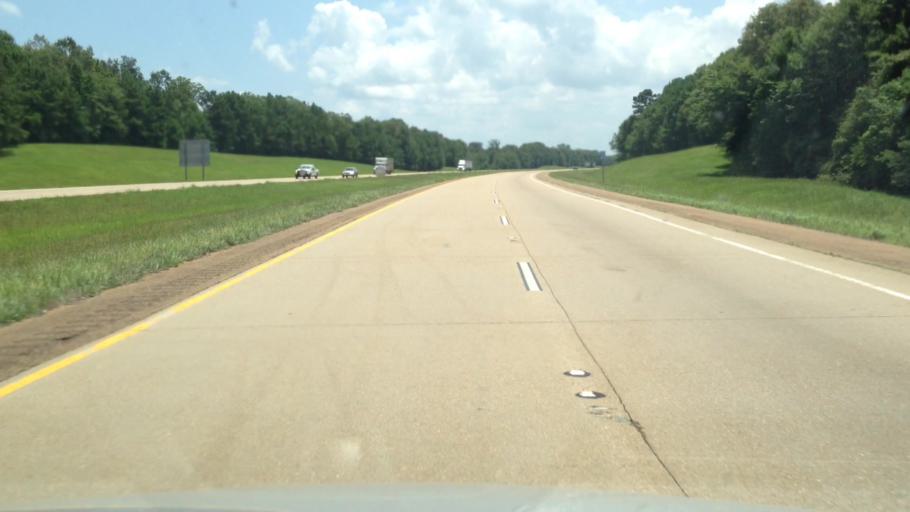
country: US
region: Louisiana
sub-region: Rapides Parish
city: Woodworth
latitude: 31.1563
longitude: -92.4553
